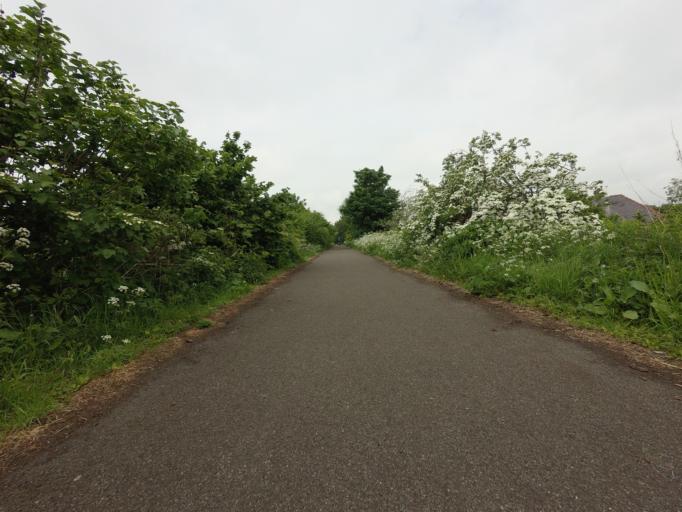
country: GB
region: Scotland
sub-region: Fife
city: Townhill
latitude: 56.0887
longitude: -3.4437
